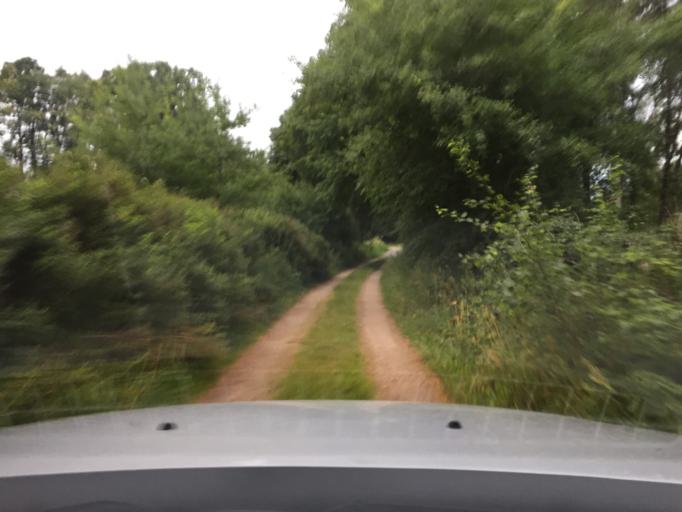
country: SE
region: Skane
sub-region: Hassleholms Kommun
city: Sosdala
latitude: 56.0395
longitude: 13.6900
